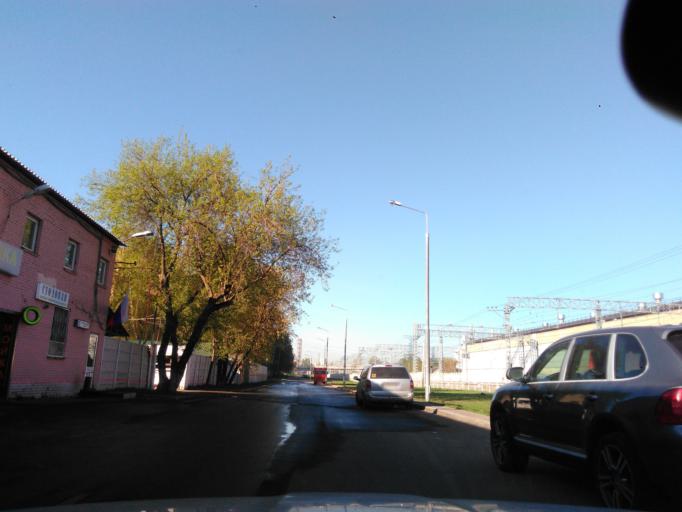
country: RU
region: Moskovskaya
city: Koptevo
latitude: 55.8352
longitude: 37.5145
